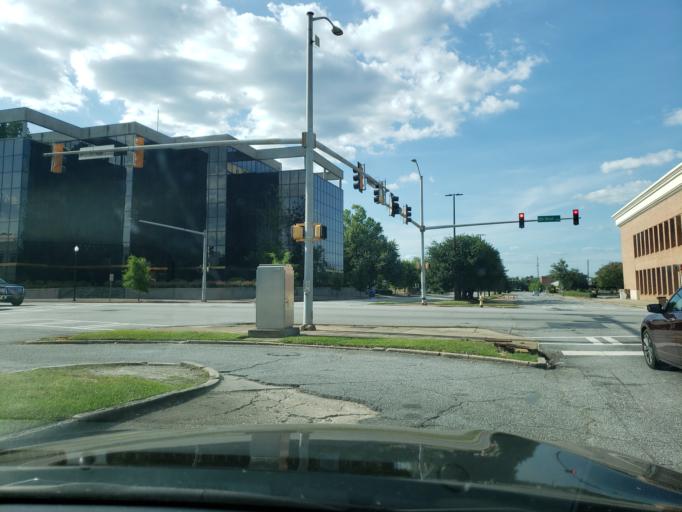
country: US
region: Alabama
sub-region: Russell County
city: Phenix City
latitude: 32.4703
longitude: -84.9917
